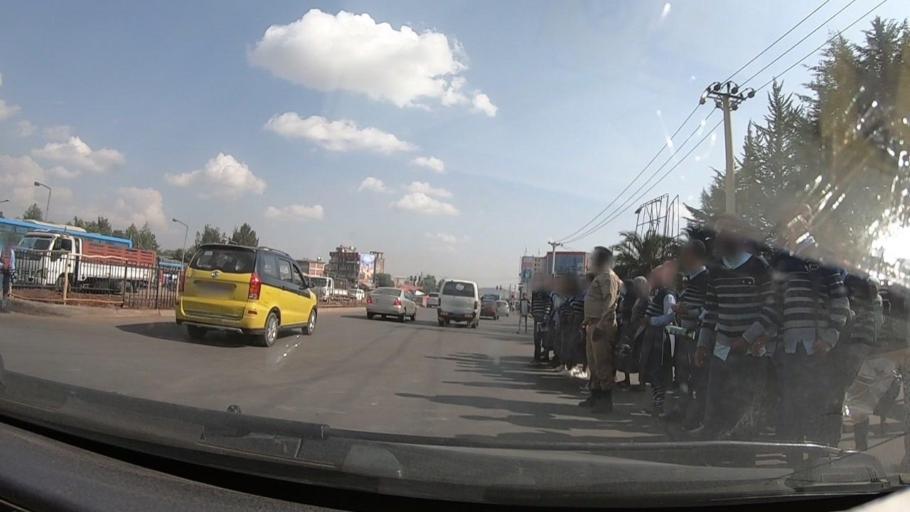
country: ET
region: Adis Abeba
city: Addis Ababa
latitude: 8.9837
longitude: 38.6962
